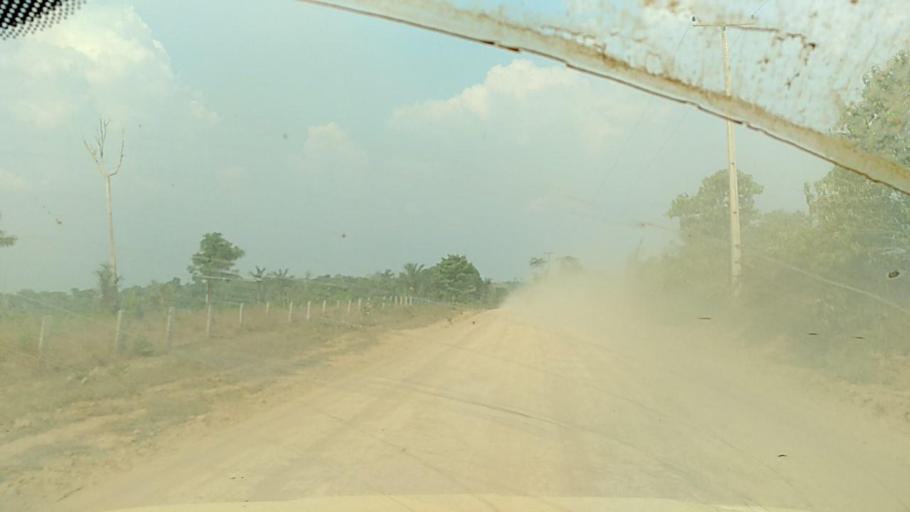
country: BR
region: Rondonia
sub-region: Porto Velho
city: Porto Velho
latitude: -8.6833
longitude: -63.1929
